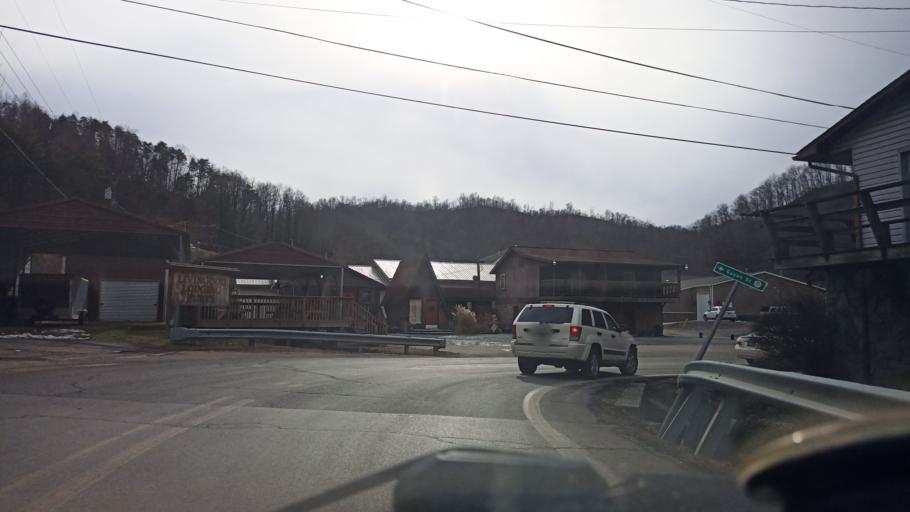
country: US
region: West Virginia
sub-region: Mingo County
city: Gilbert Creek
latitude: 37.6181
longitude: -81.8658
